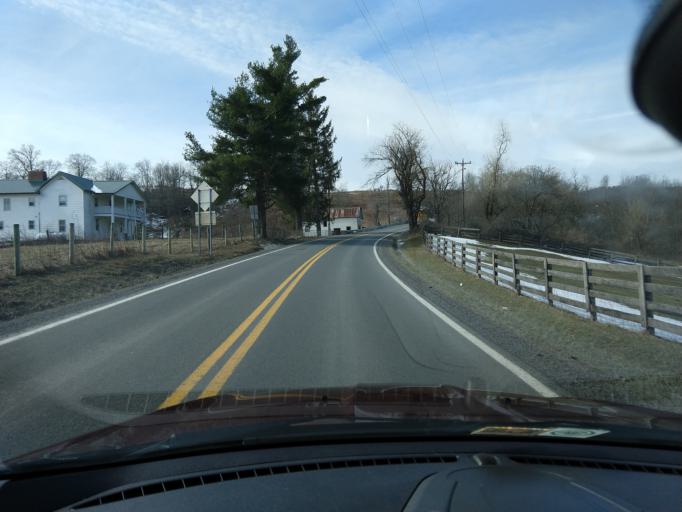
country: US
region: West Virginia
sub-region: Pocahontas County
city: Marlinton
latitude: 38.1183
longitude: -80.2438
